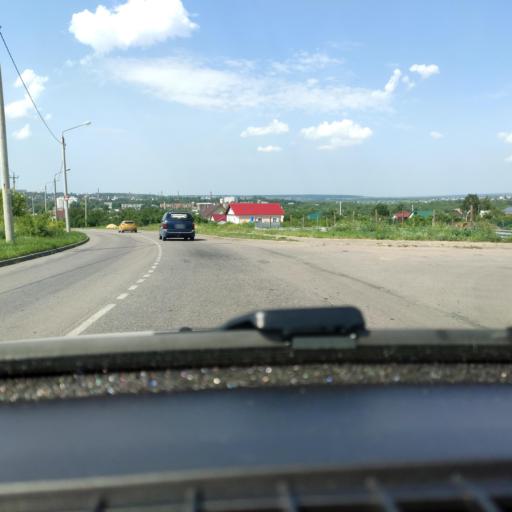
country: RU
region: Voronezj
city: Semiluki
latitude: 51.6681
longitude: 39.0377
